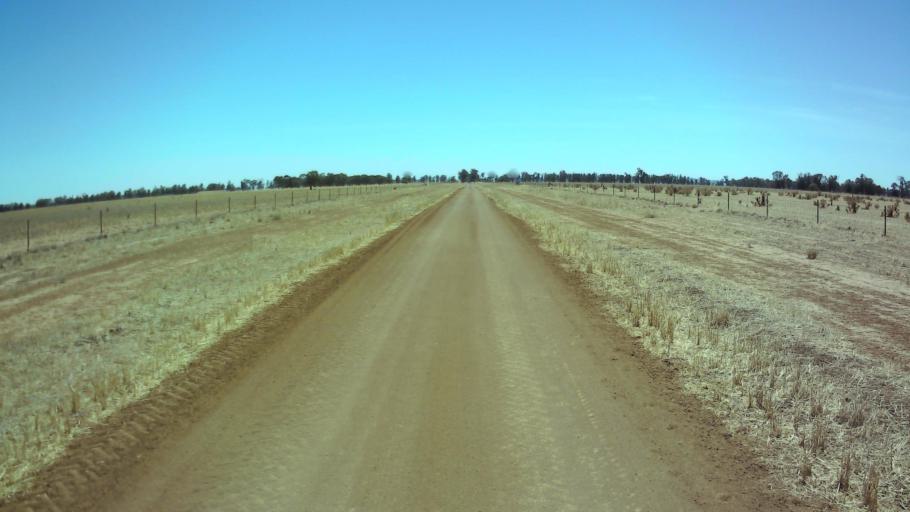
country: AU
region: New South Wales
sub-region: Weddin
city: Grenfell
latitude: -33.9831
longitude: 147.7357
